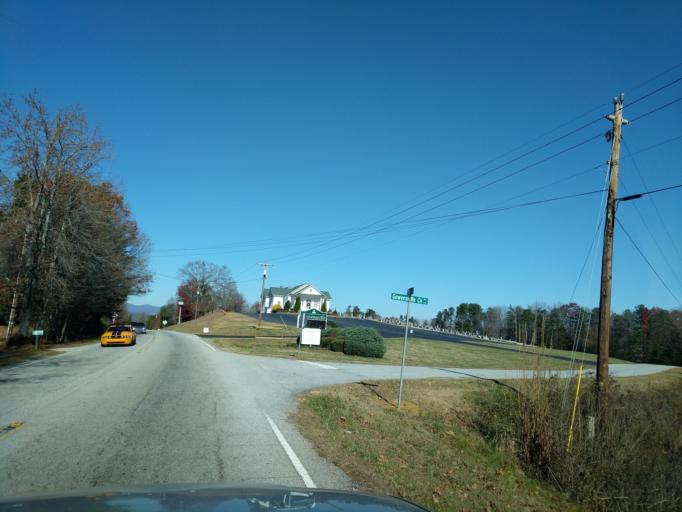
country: US
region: South Carolina
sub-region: Spartanburg County
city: Landrum
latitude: 35.1149
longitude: -82.2251
